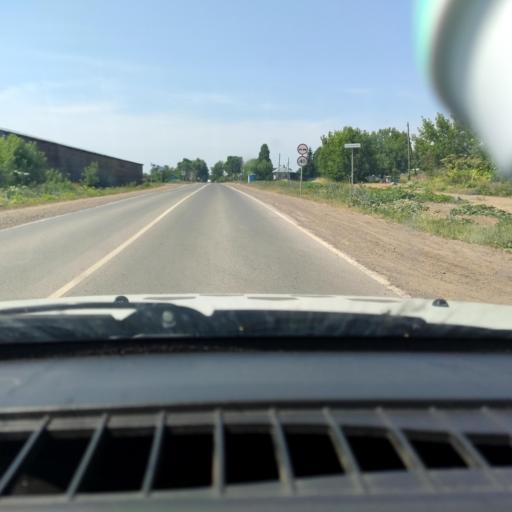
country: RU
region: Perm
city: Okhansk
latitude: 57.7105
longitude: 55.3314
